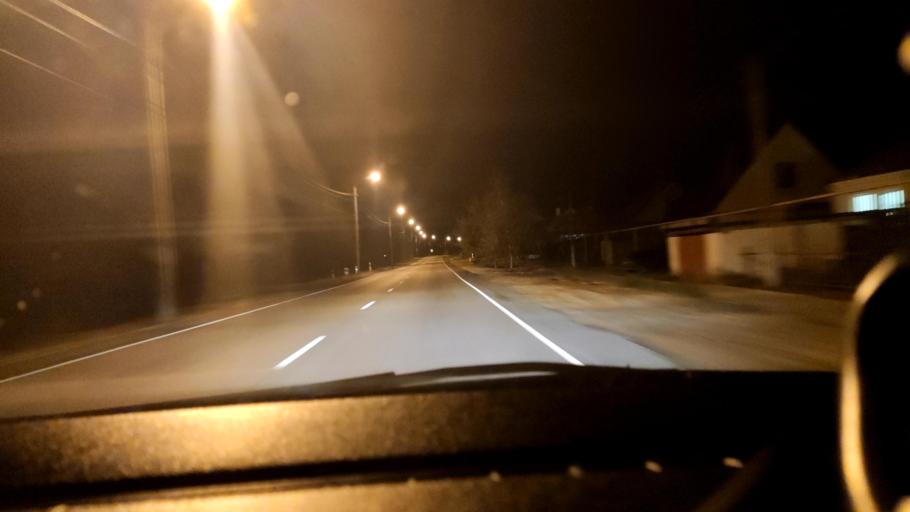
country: RU
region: Voronezj
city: Shilovo
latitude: 51.5646
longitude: 39.0521
